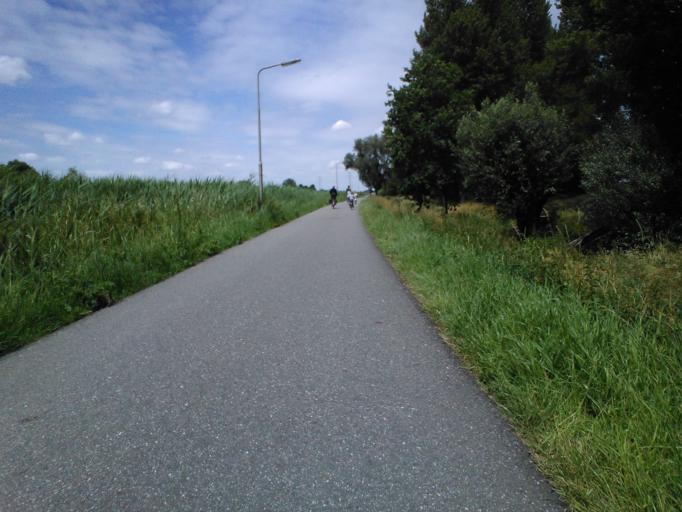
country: NL
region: South Holland
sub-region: Gemeente Alblasserdam
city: Alblasserdam
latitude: 51.8664
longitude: 4.6739
